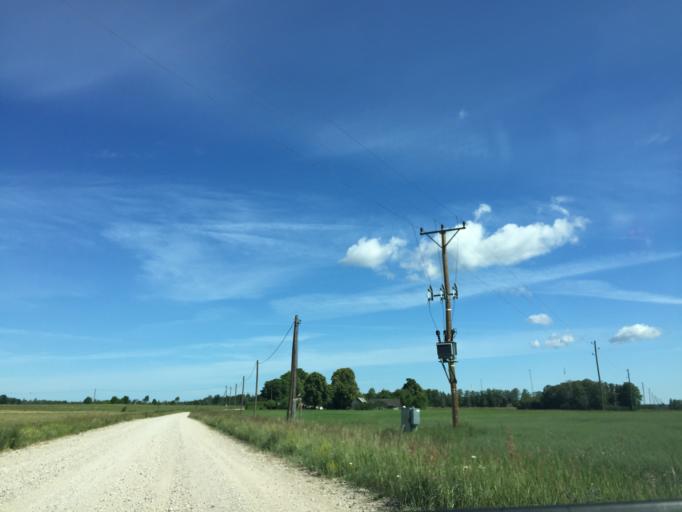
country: LV
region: Dundaga
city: Dundaga
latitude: 57.3463
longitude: 22.0266
